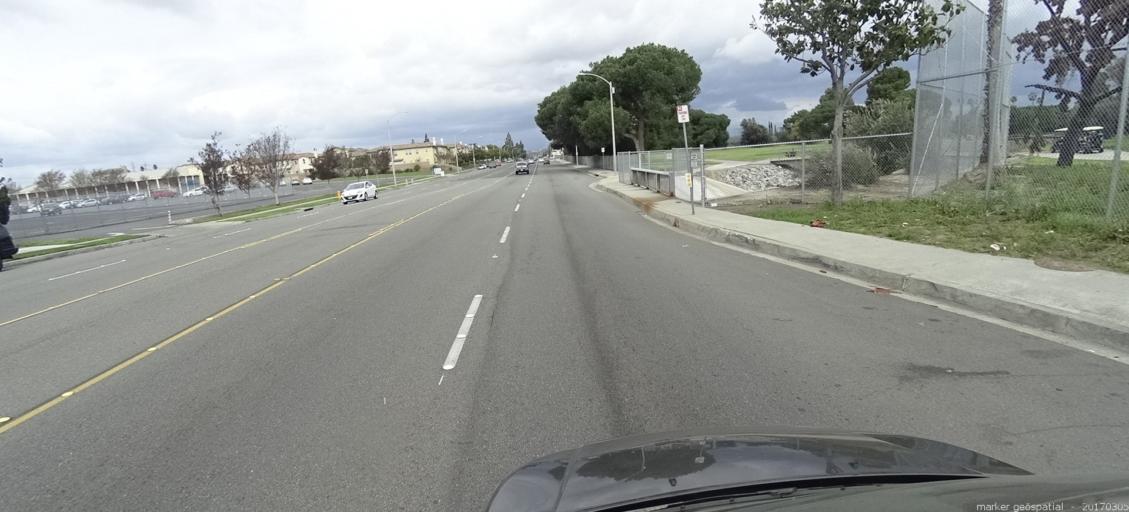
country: US
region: California
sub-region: Orange County
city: Stanton
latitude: 33.8344
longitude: -117.9760
